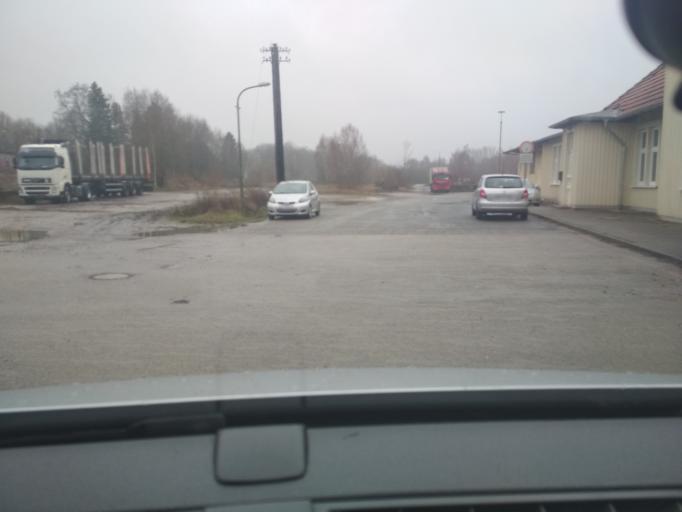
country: DE
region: Lower Saxony
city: Wittingen
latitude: 52.7274
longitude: 10.7237
